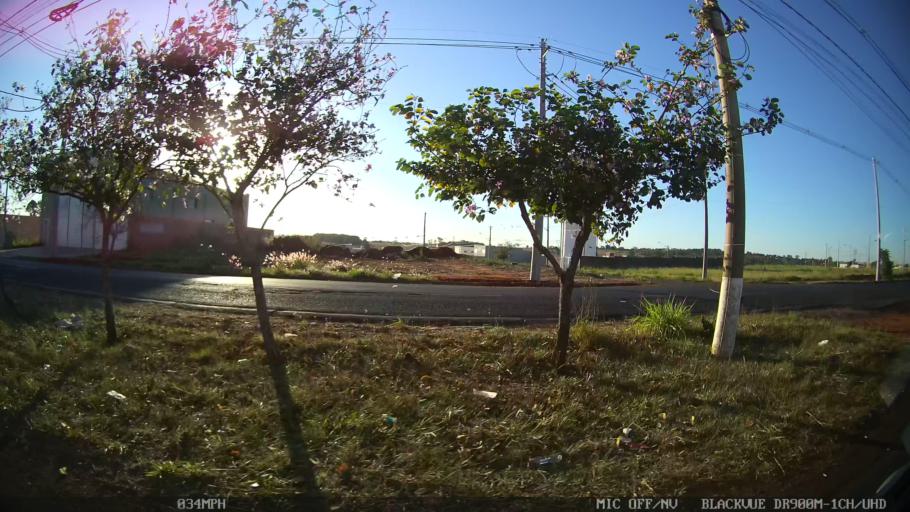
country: BR
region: Sao Paulo
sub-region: Sao Jose Do Rio Preto
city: Sao Jose do Rio Preto
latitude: -20.7625
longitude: -49.3479
